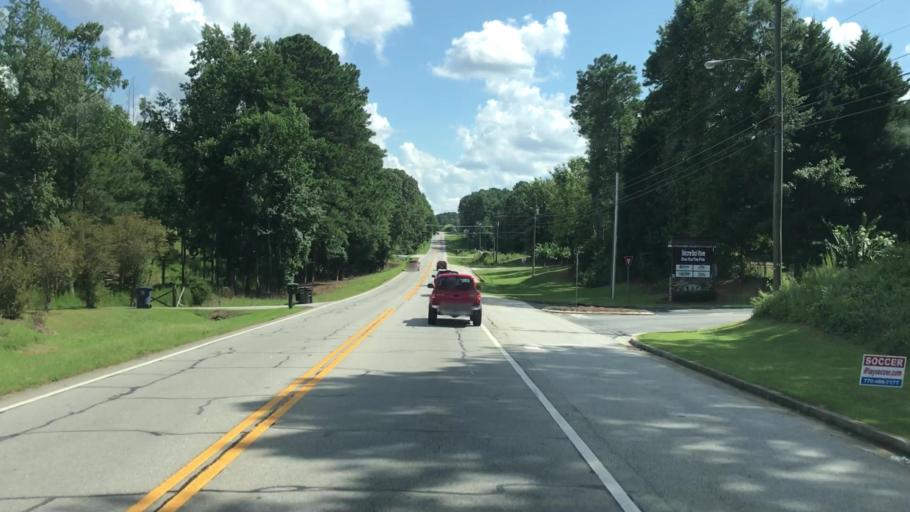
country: US
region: Georgia
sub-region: Walton County
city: Walnut Grove
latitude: 33.7293
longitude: -83.8523
